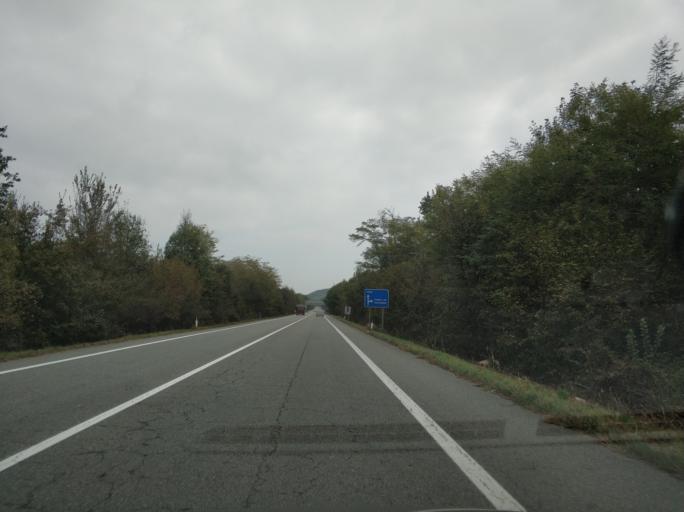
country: IT
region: Piedmont
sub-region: Provincia di Torino
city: Bairo
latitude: 45.3899
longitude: 7.7419
